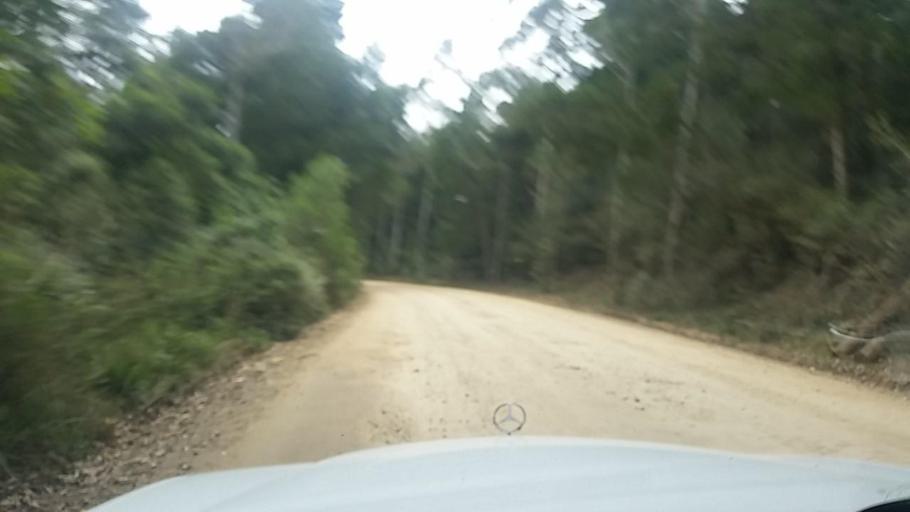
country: ZA
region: Western Cape
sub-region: Eden District Municipality
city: Knysna
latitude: -33.9842
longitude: 23.1454
